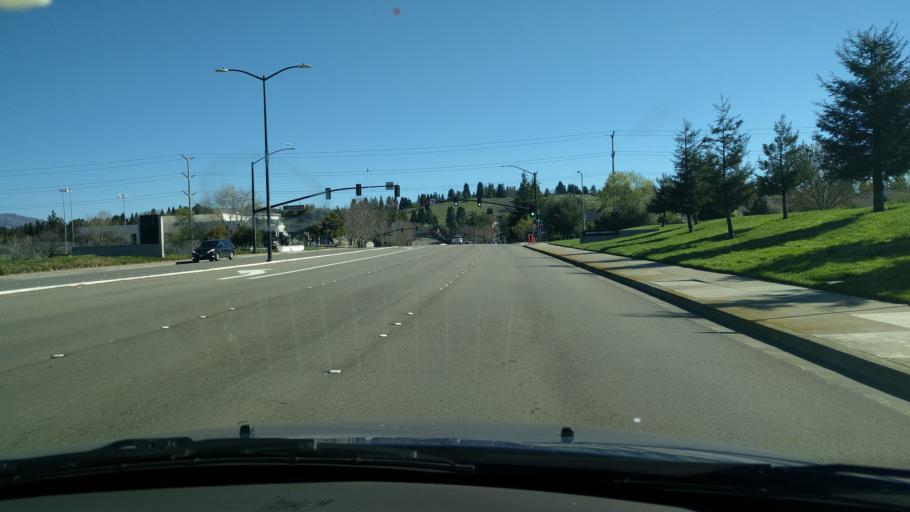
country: US
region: California
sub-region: Contra Costa County
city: San Ramon
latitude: 37.7631
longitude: -121.9560
